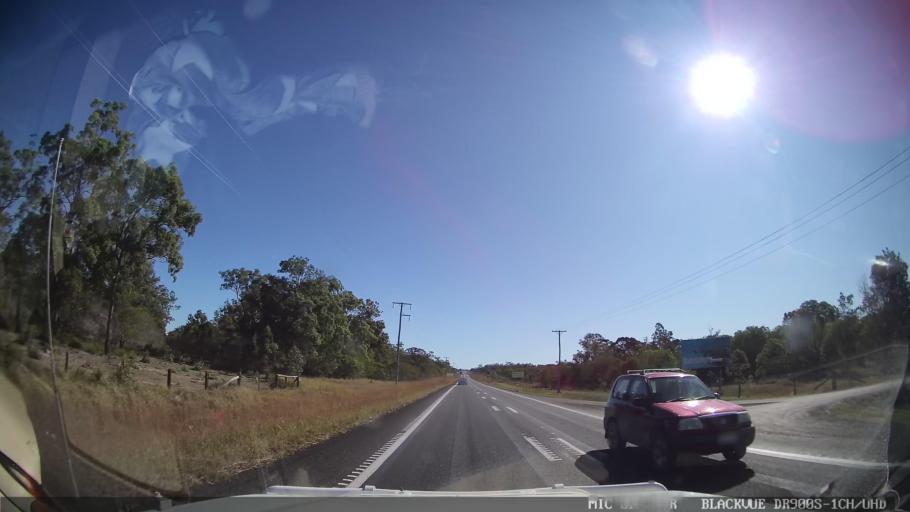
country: AU
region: Queensland
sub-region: Bundaberg
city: Childers
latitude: -25.2502
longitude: 152.3470
